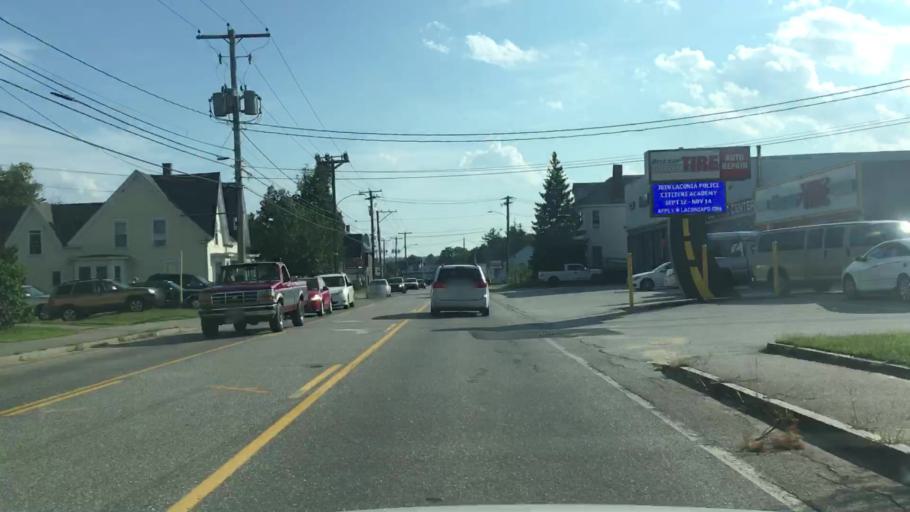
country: US
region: New Hampshire
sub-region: Belknap County
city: Laconia
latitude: 43.5455
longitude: -71.4639
